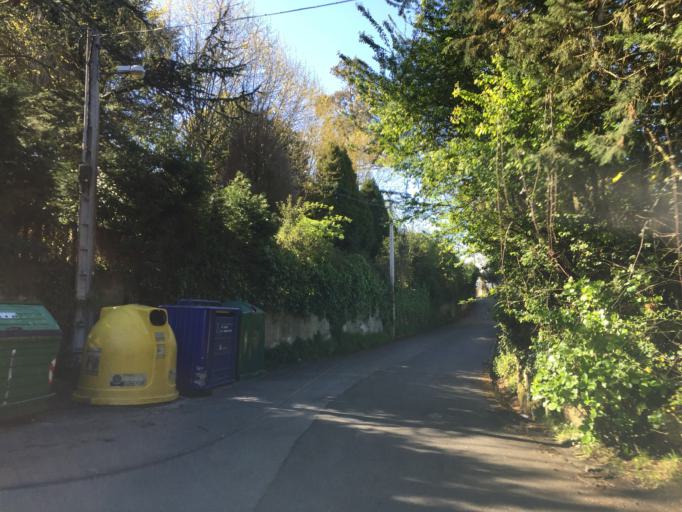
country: ES
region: Asturias
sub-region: Province of Asturias
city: Gijon
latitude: 43.5428
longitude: -5.6225
